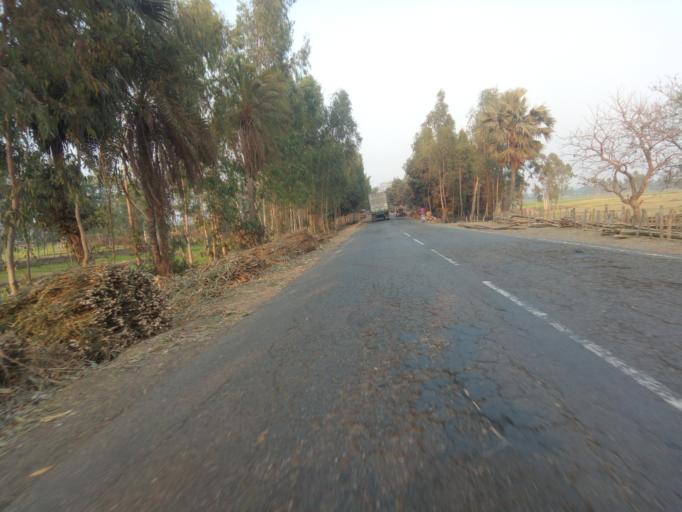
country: BD
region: Rajshahi
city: Bogra
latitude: 24.5563
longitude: 89.1974
